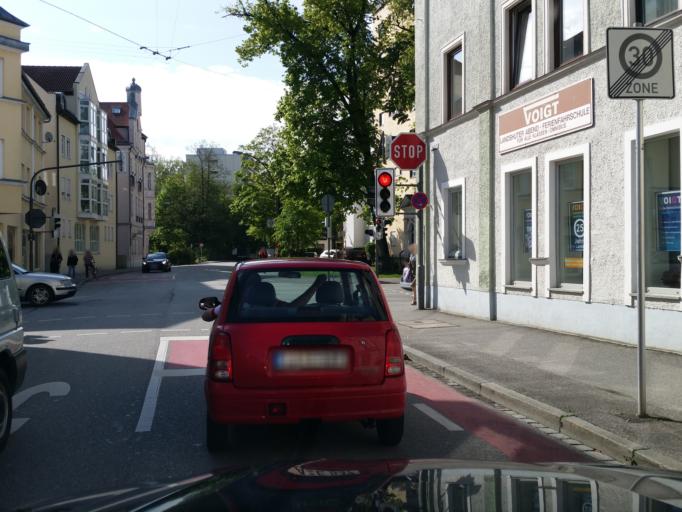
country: DE
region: Bavaria
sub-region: Lower Bavaria
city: Landshut
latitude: 48.5424
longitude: 12.1431
